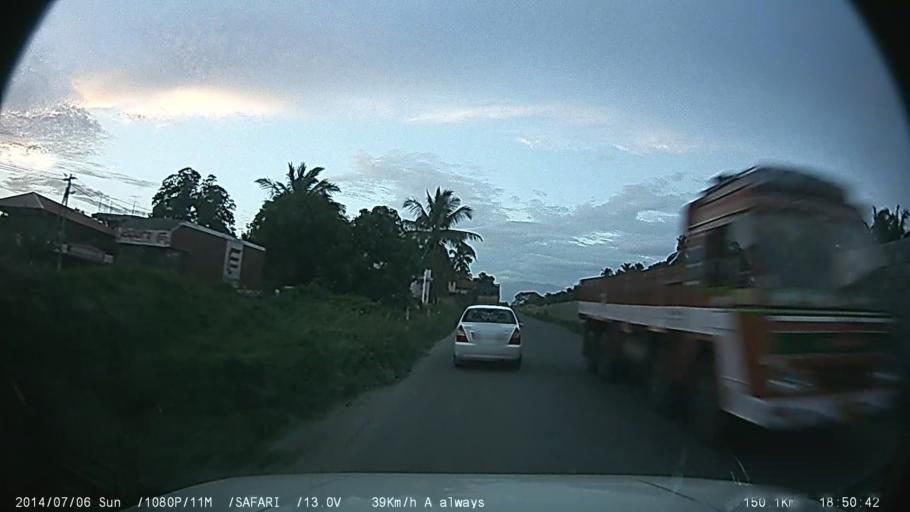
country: IN
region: Kerala
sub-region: Palakkad district
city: Palakkad
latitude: 10.7064
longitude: 76.5939
